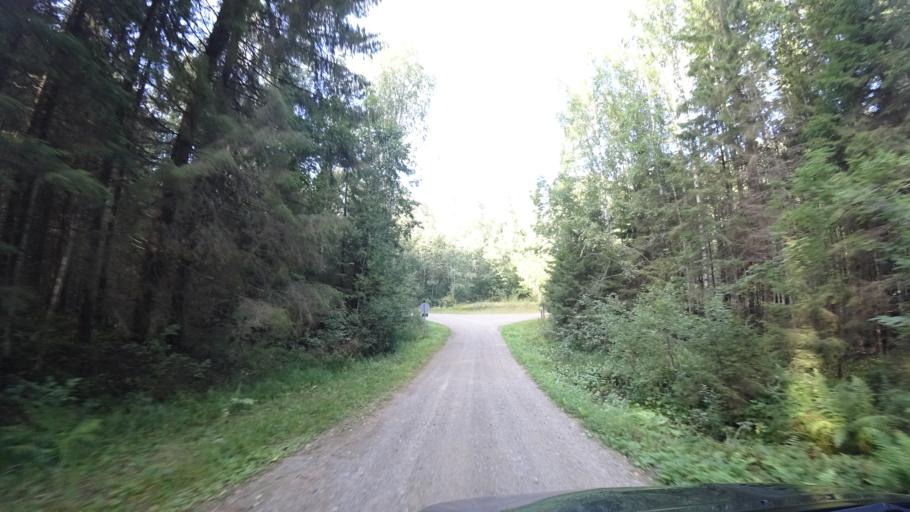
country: FI
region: Paijanne Tavastia
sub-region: Lahti
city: Auttoinen
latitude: 61.2252
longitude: 25.1934
